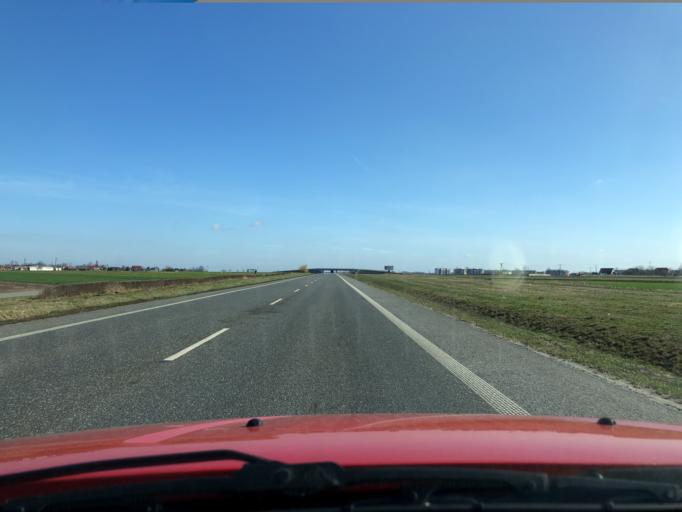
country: PL
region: Greater Poland Voivodeship
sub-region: Powiat ostrowski
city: Nowe Skalmierzyce
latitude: 51.7123
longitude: 17.9779
